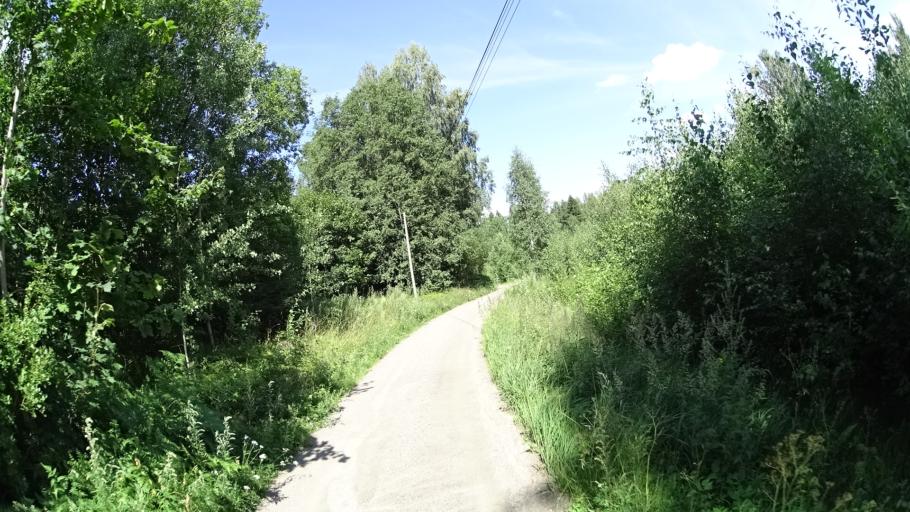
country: FI
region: Haeme
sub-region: Forssa
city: Tammela
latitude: 60.7669
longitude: 23.8717
